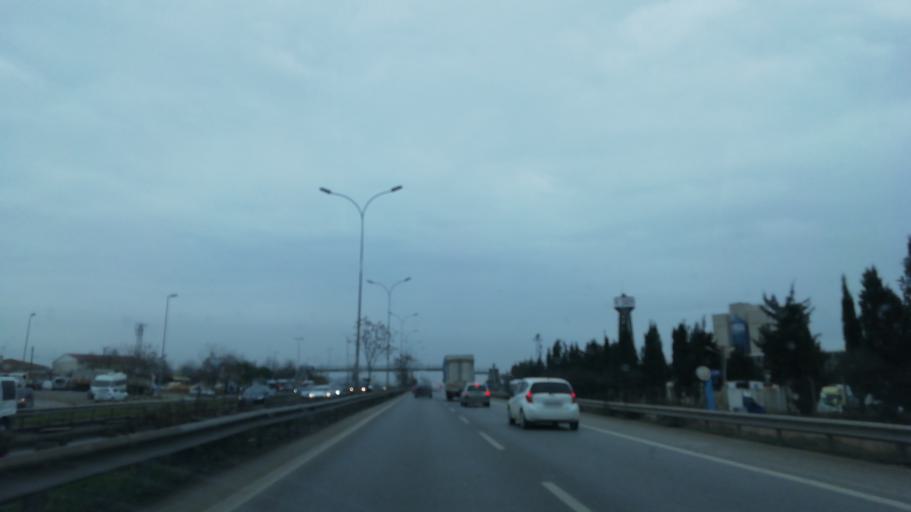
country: TR
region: Istanbul
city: Icmeler
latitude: 40.8238
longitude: 29.3514
